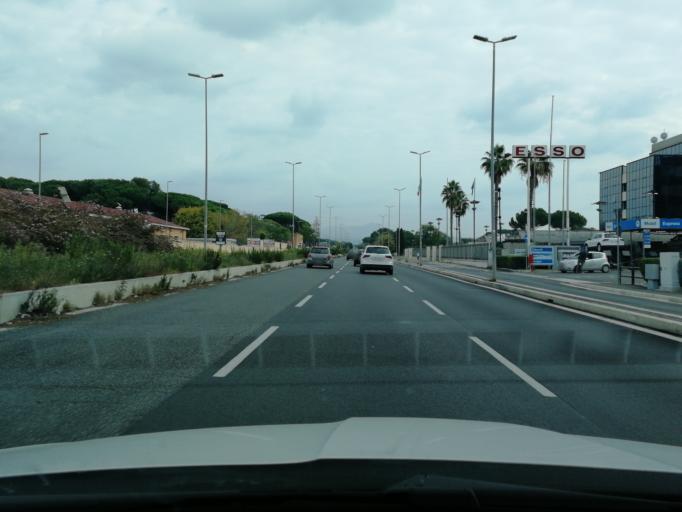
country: IT
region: Latium
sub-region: Citta metropolitana di Roma Capitale
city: Ciampino
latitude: 41.8511
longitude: 12.5717
